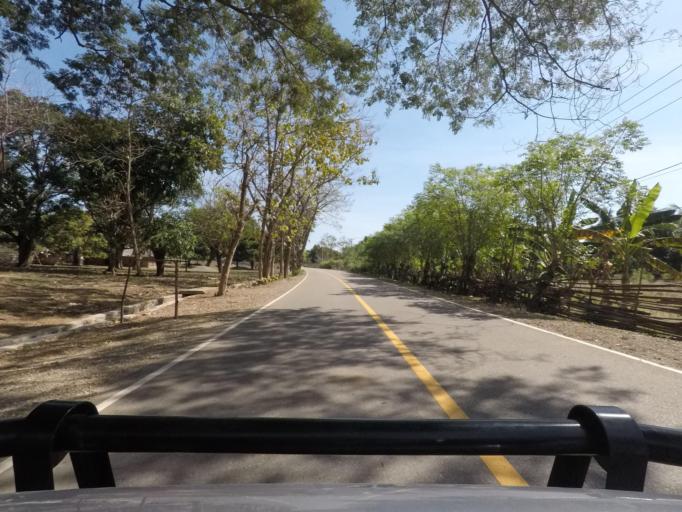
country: TL
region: Bobonaro
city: Maliana
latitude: -8.8799
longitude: 125.0337
